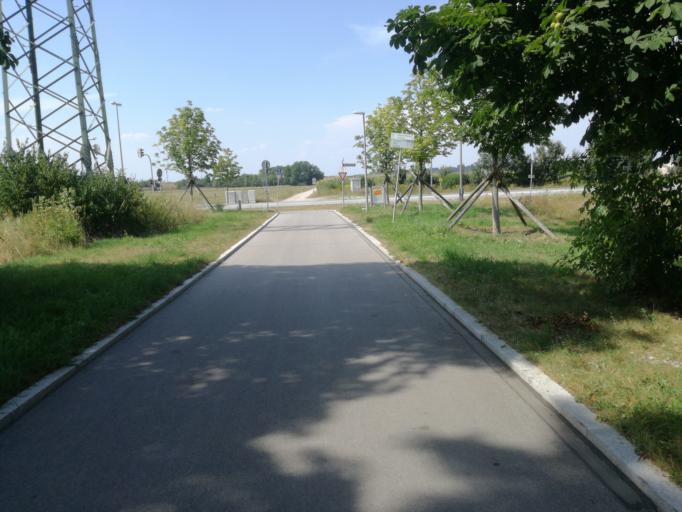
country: DE
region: Bavaria
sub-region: Upper Bavaria
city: Germering
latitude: 48.1389
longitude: 11.4009
